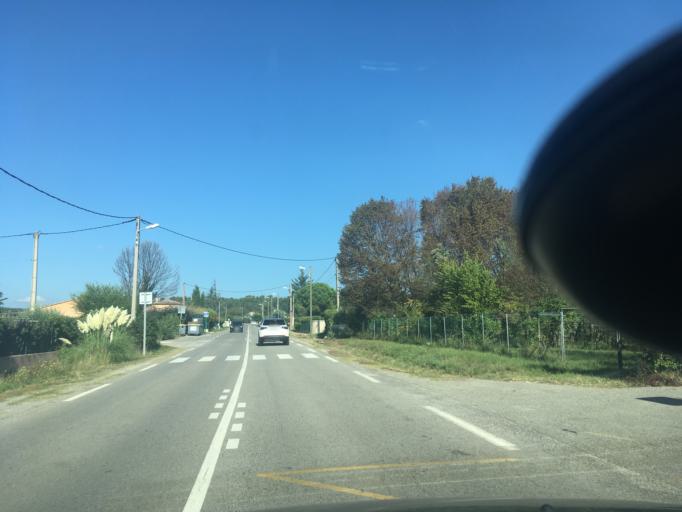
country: FR
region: Provence-Alpes-Cote d'Azur
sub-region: Departement du Var
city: Regusse
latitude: 43.6548
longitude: 6.1436
